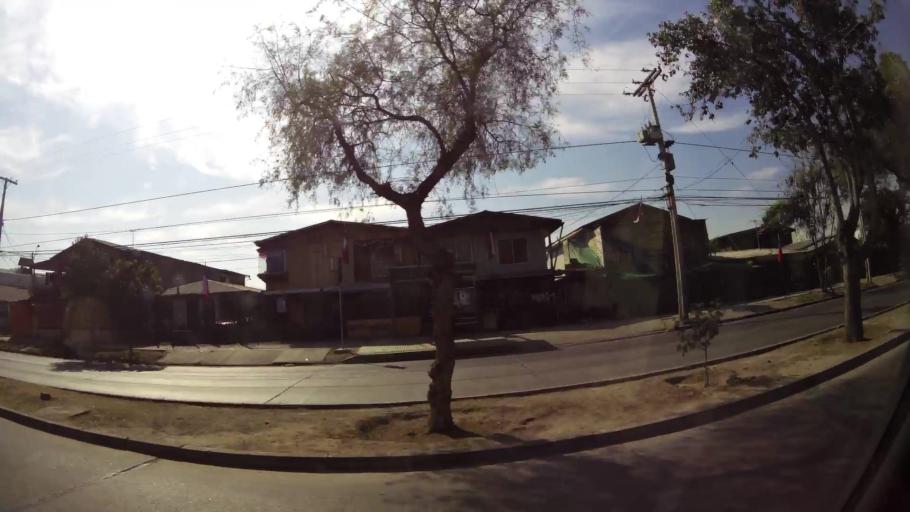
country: CL
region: Santiago Metropolitan
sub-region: Provincia de Santiago
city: Lo Prado
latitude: -33.4511
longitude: -70.7392
